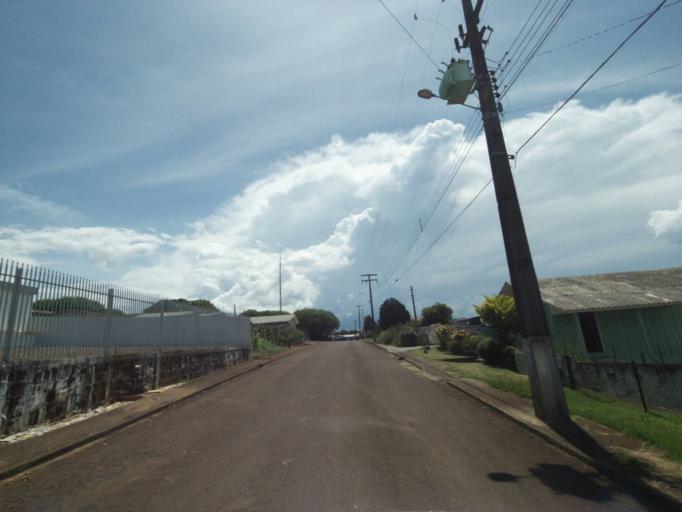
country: BR
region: Parana
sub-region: Guaraniacu
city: Guaraniacu
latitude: -25.0940
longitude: -52.8743
